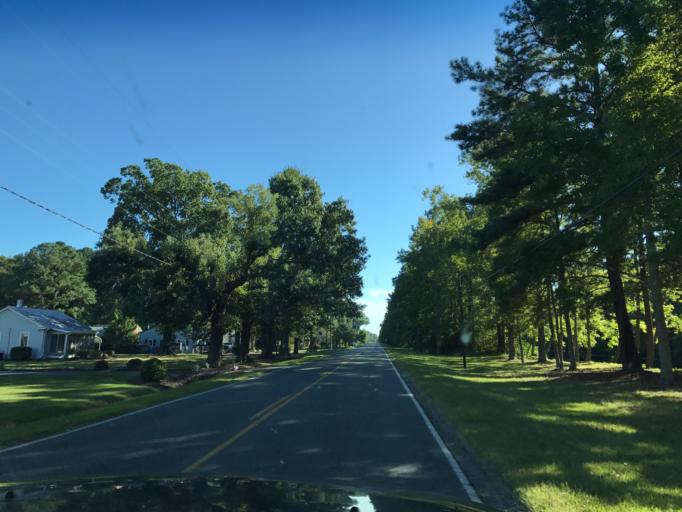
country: US
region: Virginia
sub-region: City of Portsmouth
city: Portsmouth Heights
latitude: 36.7330
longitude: -76.3467
